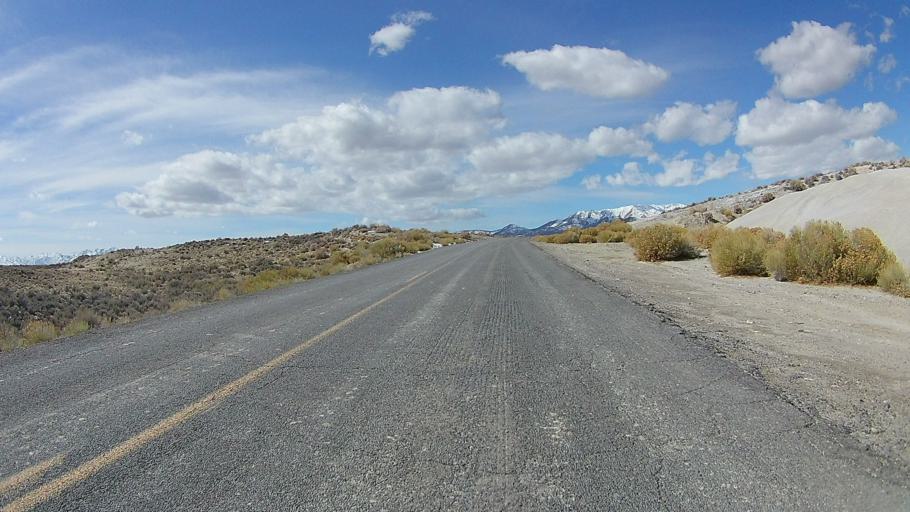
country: US
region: Utah
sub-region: Tooele County
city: Tooele
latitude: 40.1833
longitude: -112.3861
